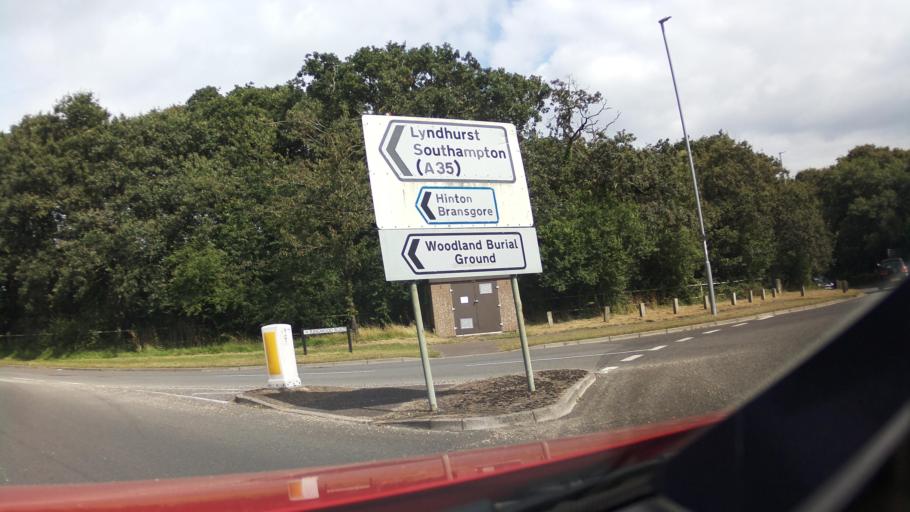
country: GB
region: England
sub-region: Hampshire
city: New Milton
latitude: 50.7451
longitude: -1.6889
